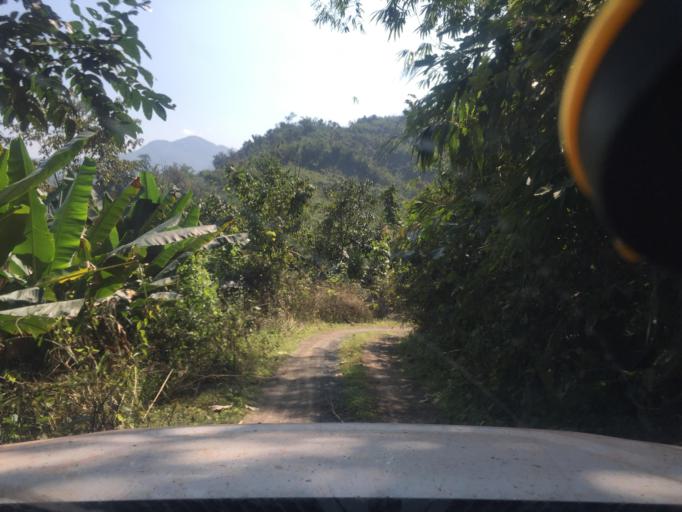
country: LA
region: Phongsali
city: Phongsali
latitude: 21.6869
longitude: 102.4088
